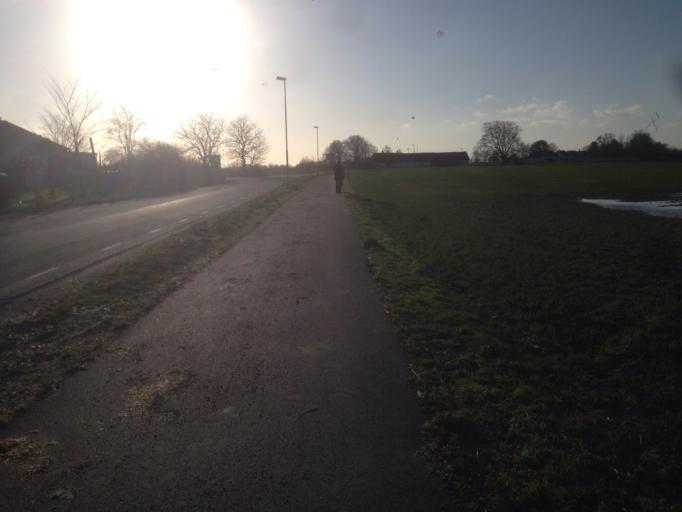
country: SE
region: Skane
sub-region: Vellinge Kommun
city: Hollviken
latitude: 55.4065
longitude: 13.0011
